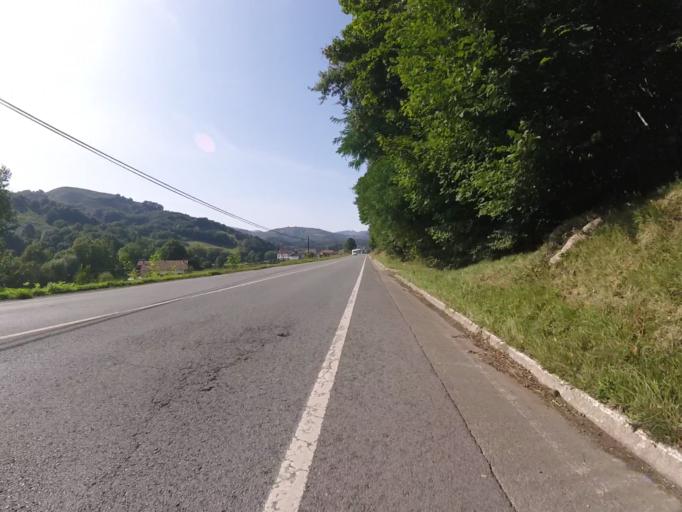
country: ES
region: Navarre
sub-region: Provincia de Navarra
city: Zugarramurdi
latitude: 43.1555
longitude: -1.5022
